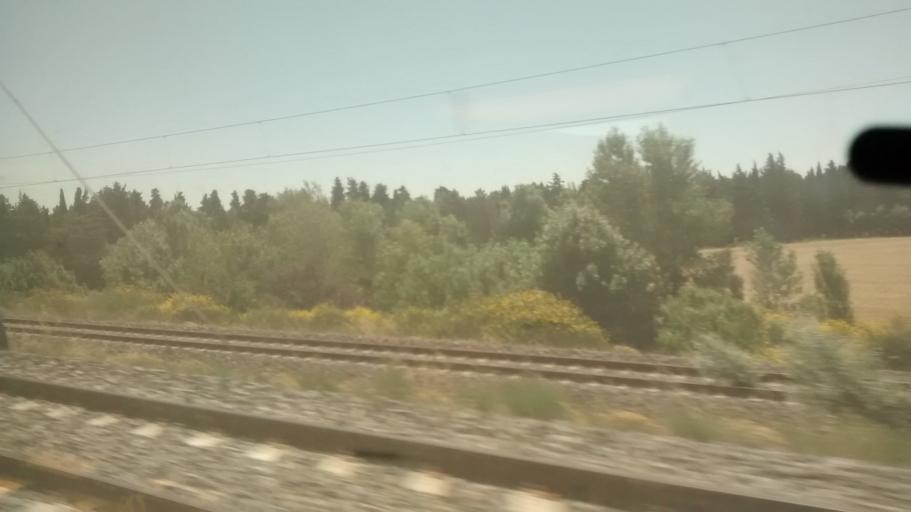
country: FR
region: Provence-Alpes-Cote d'Azur
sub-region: Departement du Vaucluse
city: Piolenc
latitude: 44.1516
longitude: 4.7497
